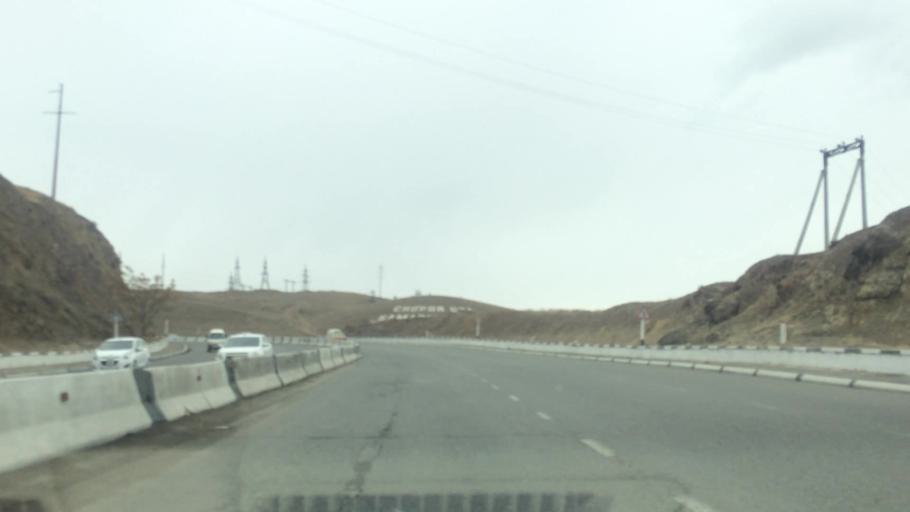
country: UZ
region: Samarqand
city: Jomboy
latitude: 39.6893
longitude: 67.0545
